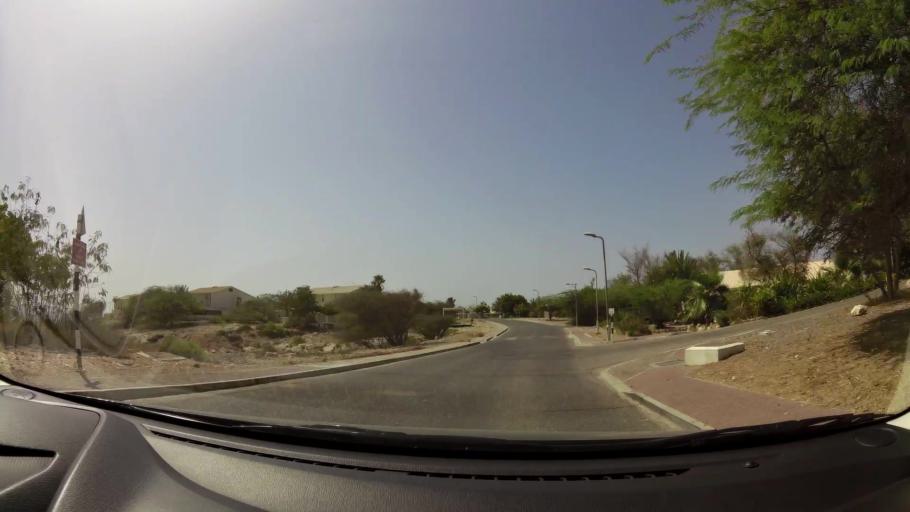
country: OM
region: Muhafazat Masqat
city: Muscat
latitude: 23.6332
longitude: 58.4972
